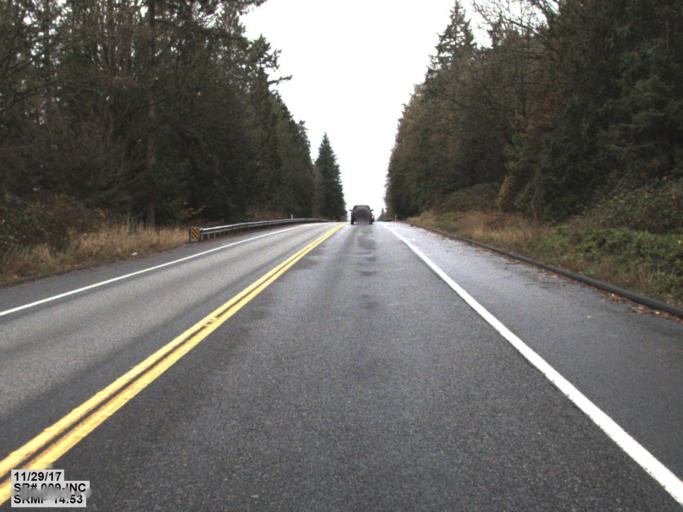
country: US
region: Washington
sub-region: Snohomish County
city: West Lake Stevens
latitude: 47.9852
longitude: -122.1034
